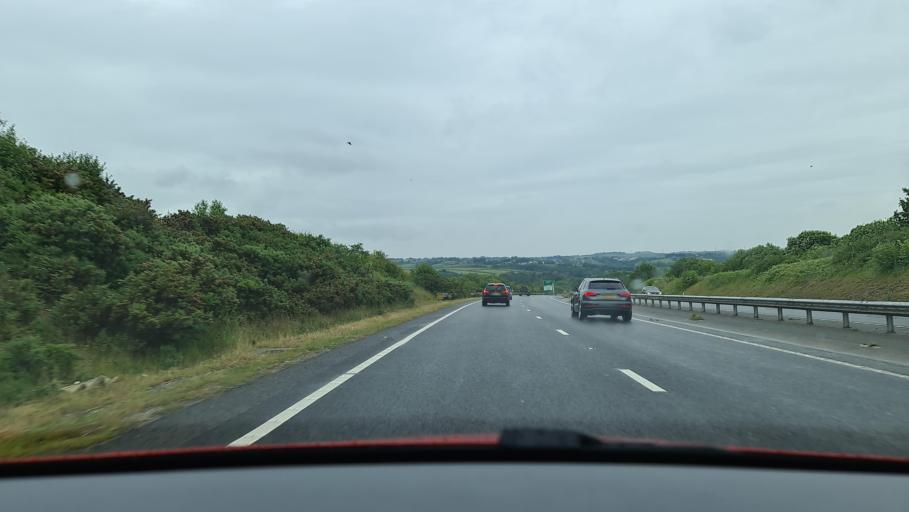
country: GB
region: England
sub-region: Cornwall
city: Liskeard
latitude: 50.4603
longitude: -4.5136
